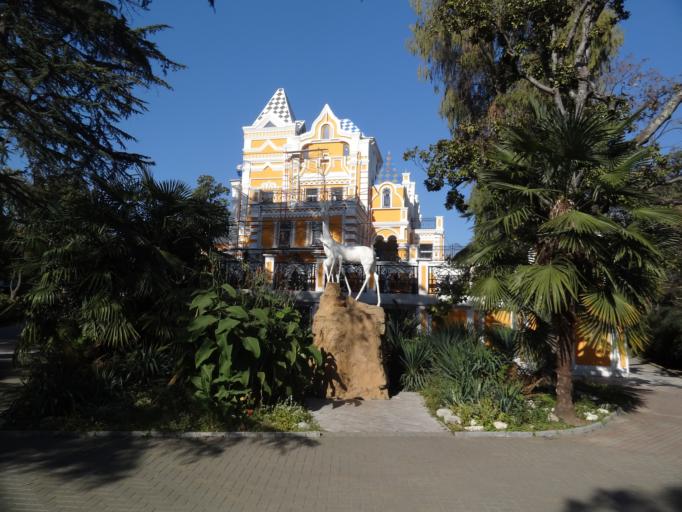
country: RU
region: Krasnodarskiy
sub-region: Sochi City
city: Sochi
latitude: 43.5898
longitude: 39.7149
